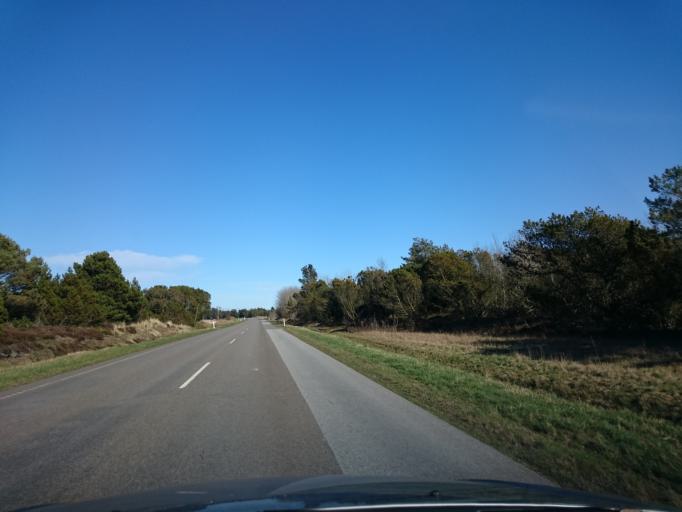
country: DK
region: North Denmark
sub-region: Frederikshavn Kommune
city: Strandby
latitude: 57.6055
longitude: 10.3725
